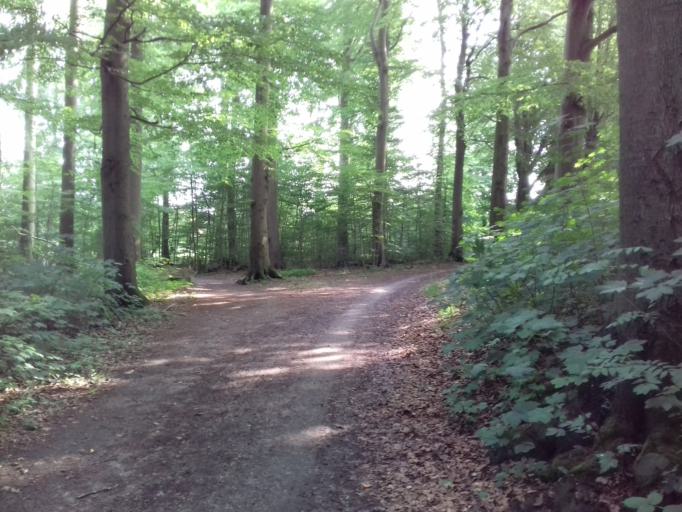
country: DE
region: Schleswig-Holstein
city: Kronshagen
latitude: 54.3213
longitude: 10.0674
